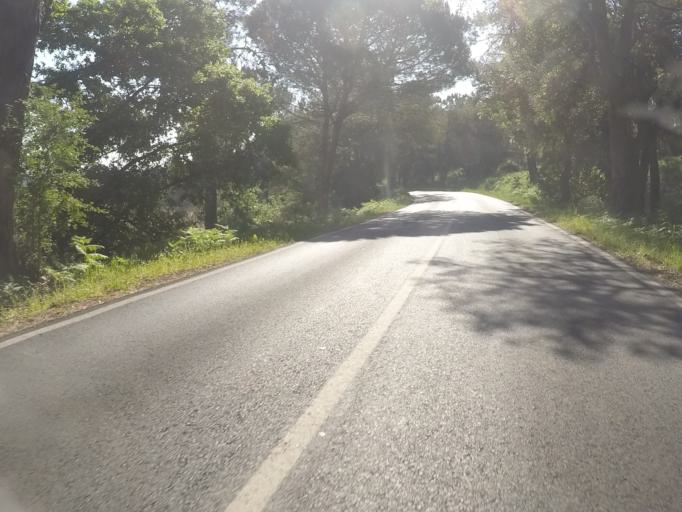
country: PT
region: Setubal
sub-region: Sesimbra
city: Sesimbra
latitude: 38.5265
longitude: -9.1379
